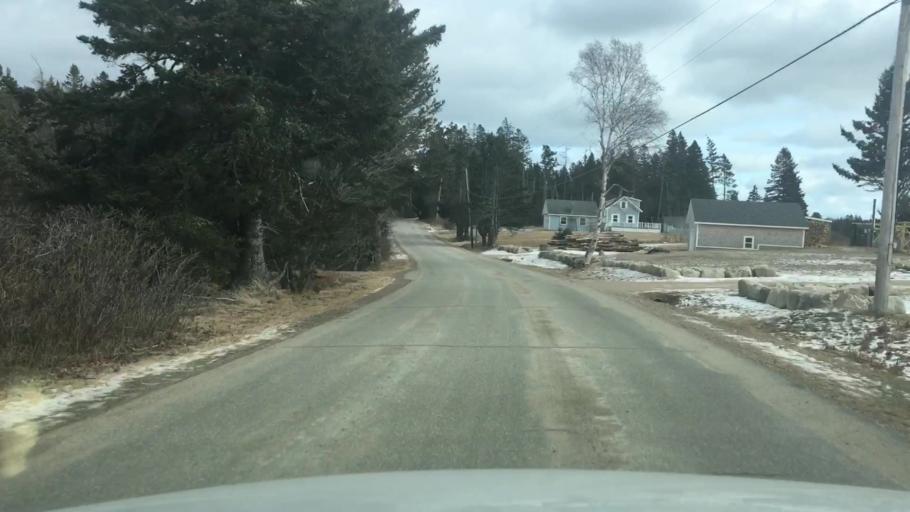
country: US
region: Maine
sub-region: Washington County
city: Machias
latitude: 44.6087
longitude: -67.4741
